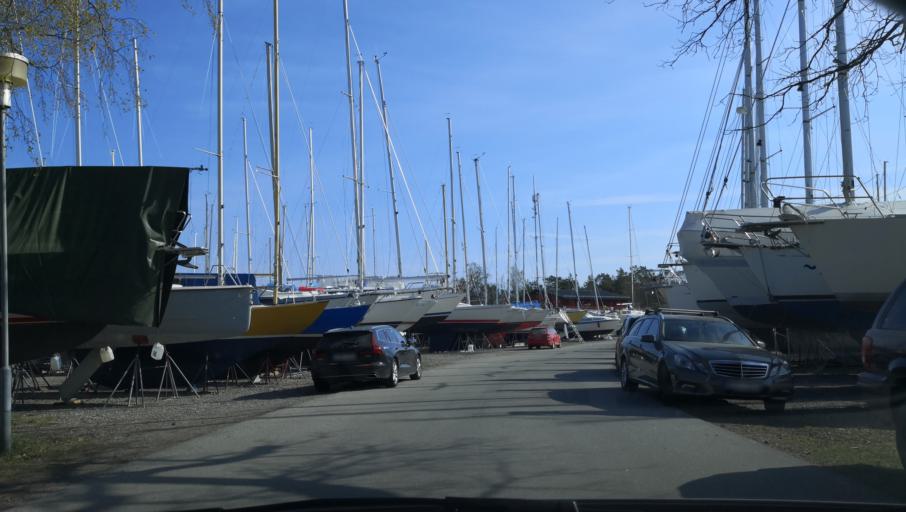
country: SE
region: Stockholm
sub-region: Varmdo Kommun
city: Holo
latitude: 59.3014
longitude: 18.6506
